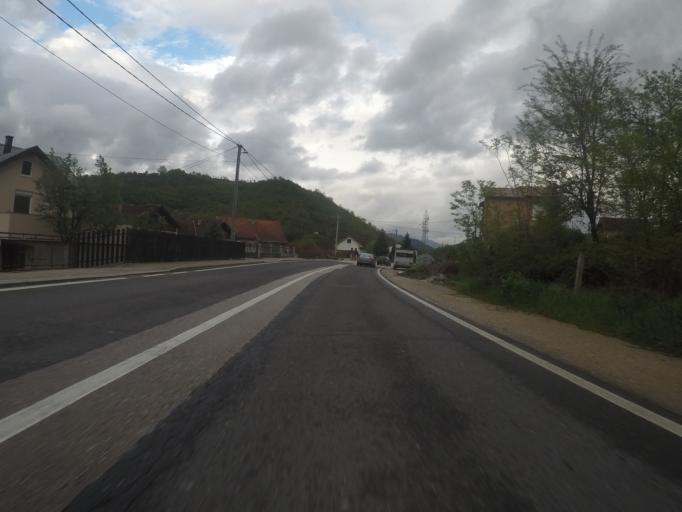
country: BA
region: Federation of Bosnia and Herzegovina
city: Konjic
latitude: 43.6820
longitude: 17.9036
